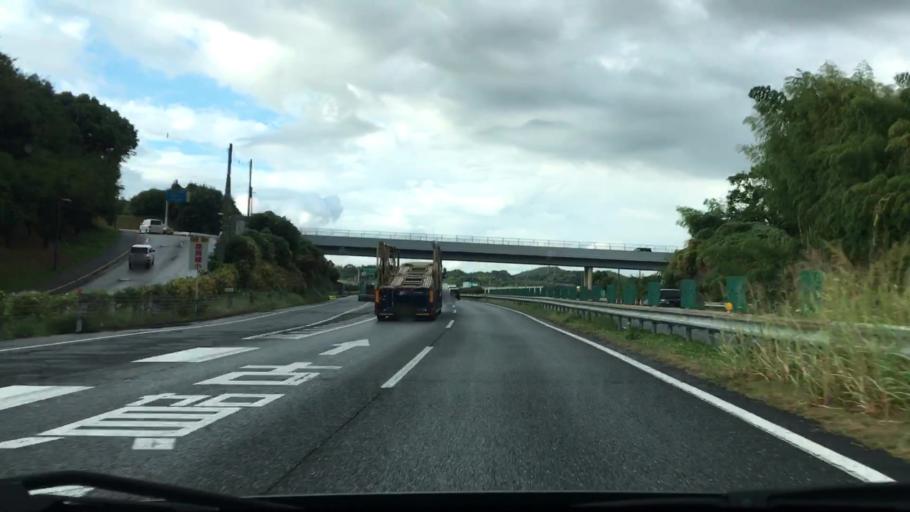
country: JP
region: Fukuoka
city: Koga
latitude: 33.7104
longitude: 130.4887
